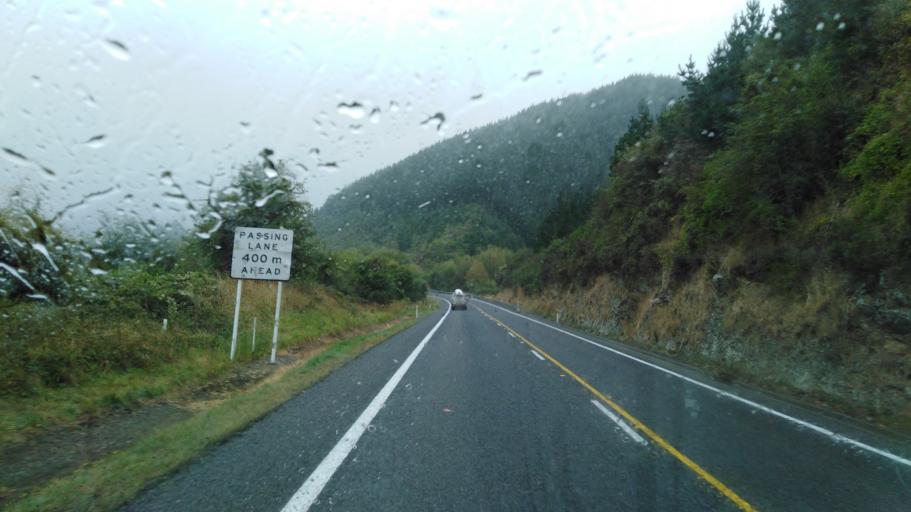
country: NZ
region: Marlborough
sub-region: Marlborough District
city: Picton
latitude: -41.3881
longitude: 173.9519
